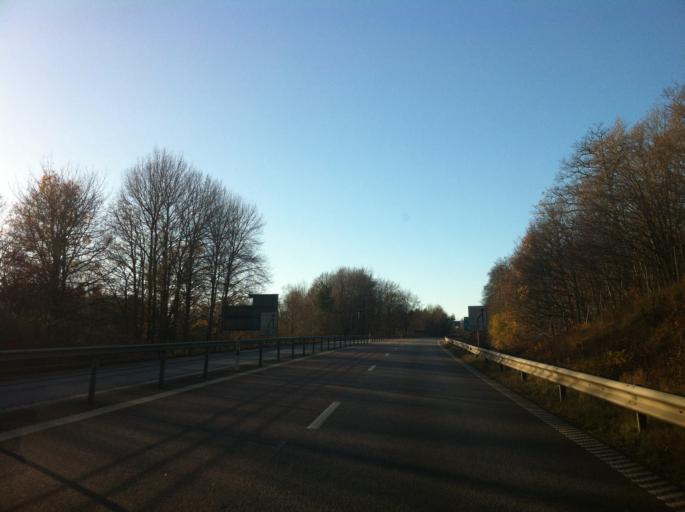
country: SE
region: Blekinge
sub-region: Karlshamns Kommun
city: Karlshamn
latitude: 56.1868
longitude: 14.8380
